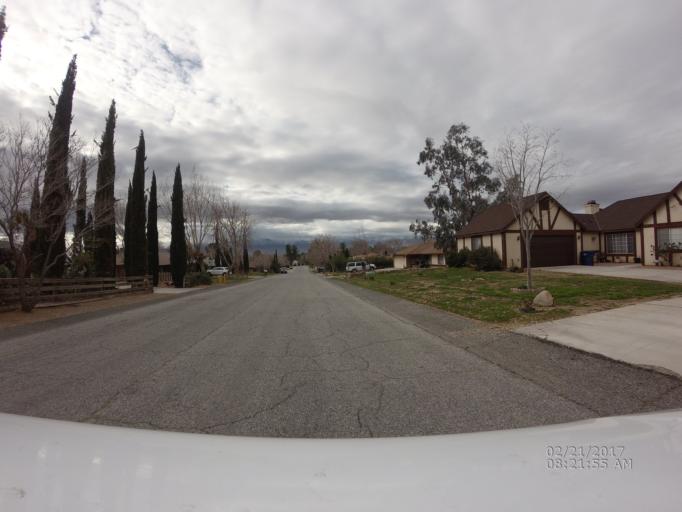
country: US
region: California
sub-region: Los Angeles County
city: Lake Los Angeles
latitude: 34.6000
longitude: -117.8403
